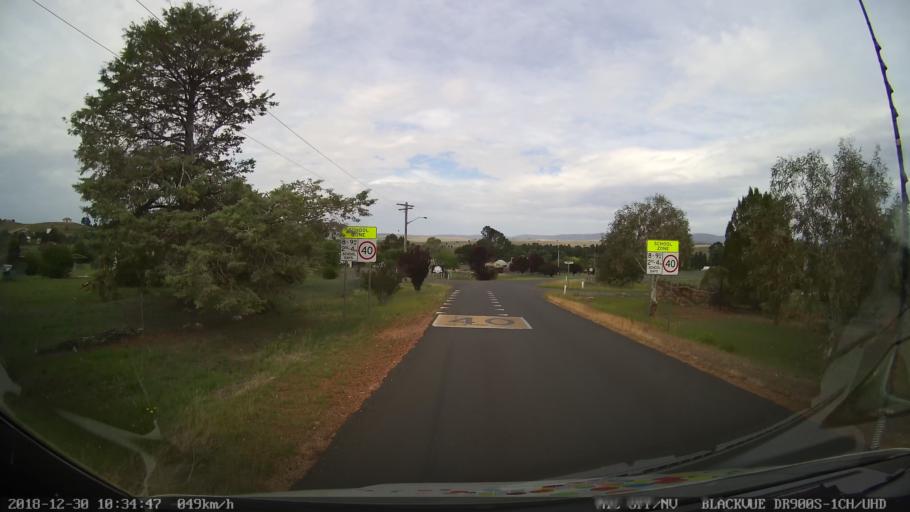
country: AU
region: New South Wales
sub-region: Snowy River
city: Berridale
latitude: -36.5017
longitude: 148.8382
